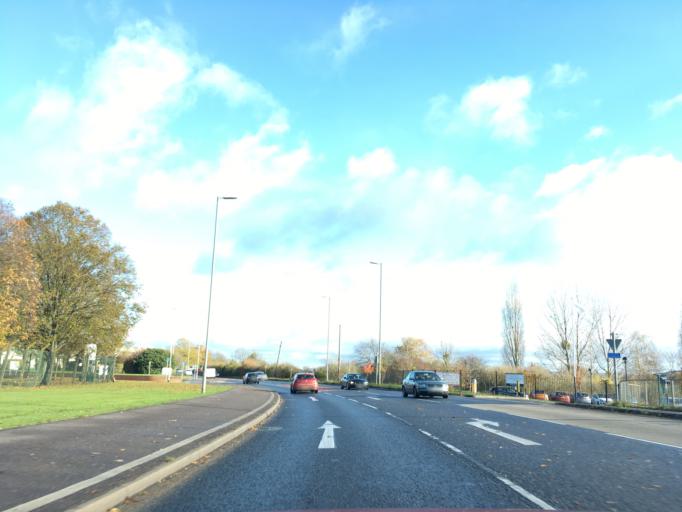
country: GB
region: England
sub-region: Worcestershire
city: Bredon
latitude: 51.9980
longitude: -2.1006
